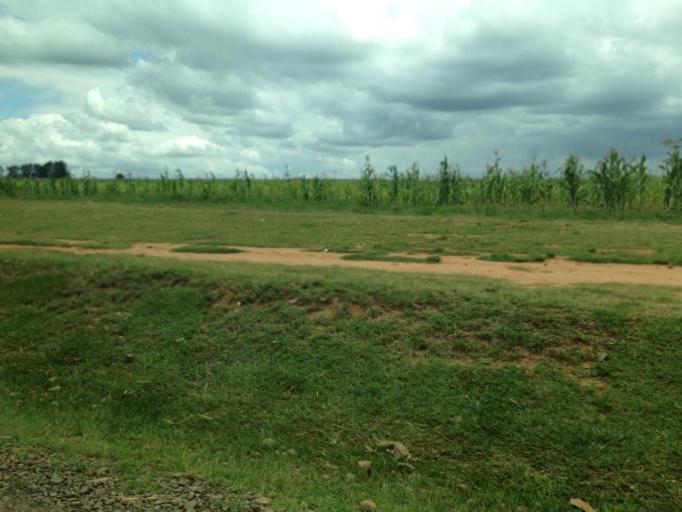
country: LS
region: Leribe
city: Leribe
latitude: -28.9323
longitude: 28.1533
